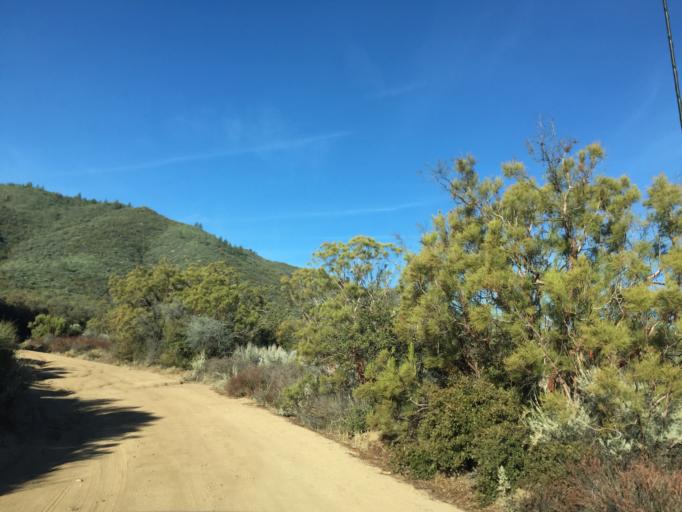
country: US
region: California
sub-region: Riverside County
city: Anza
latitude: 33.5880
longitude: -116.7608
